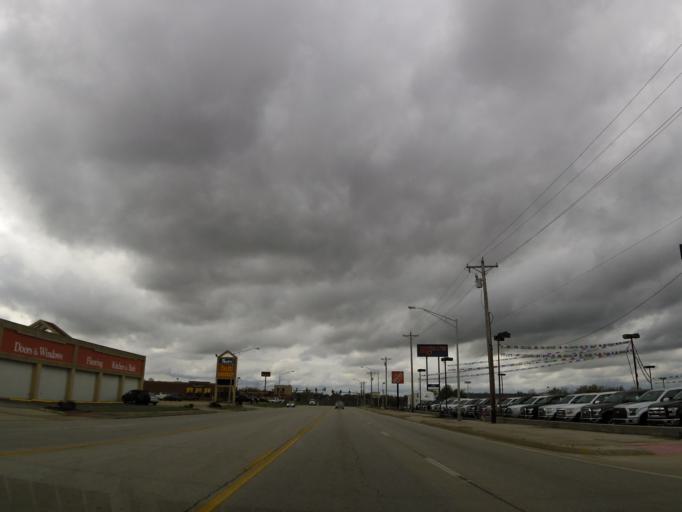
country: US
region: Missouri
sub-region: Butler County
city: Poplar Bluff
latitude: 36.7503
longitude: -90.4101
